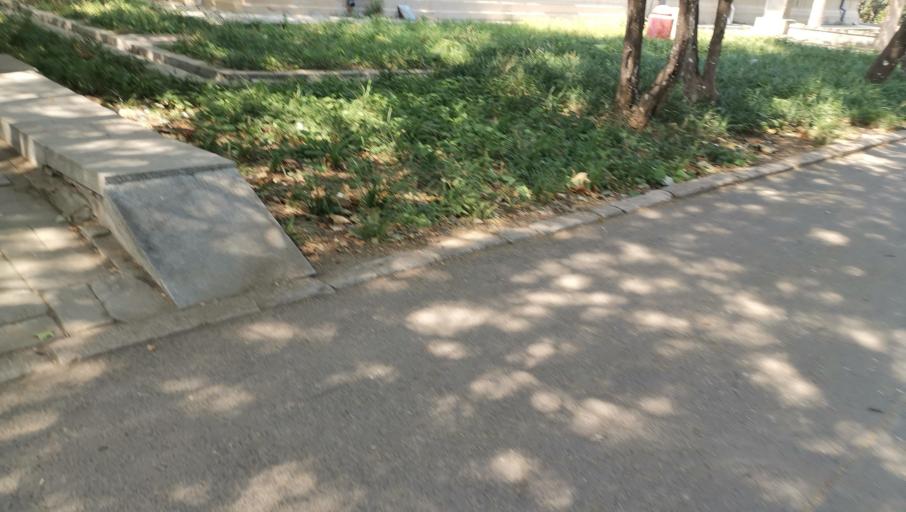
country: CN
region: Shandong Sheng
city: Jinan
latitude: 36.6517
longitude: 117.0127
